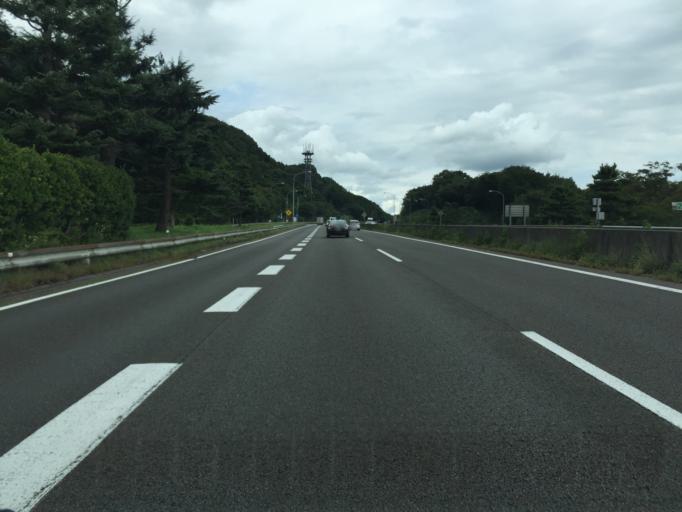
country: JP
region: Fukushima
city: Yanagawamachi-saiwaicho
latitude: 37.9077
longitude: 140.5787
